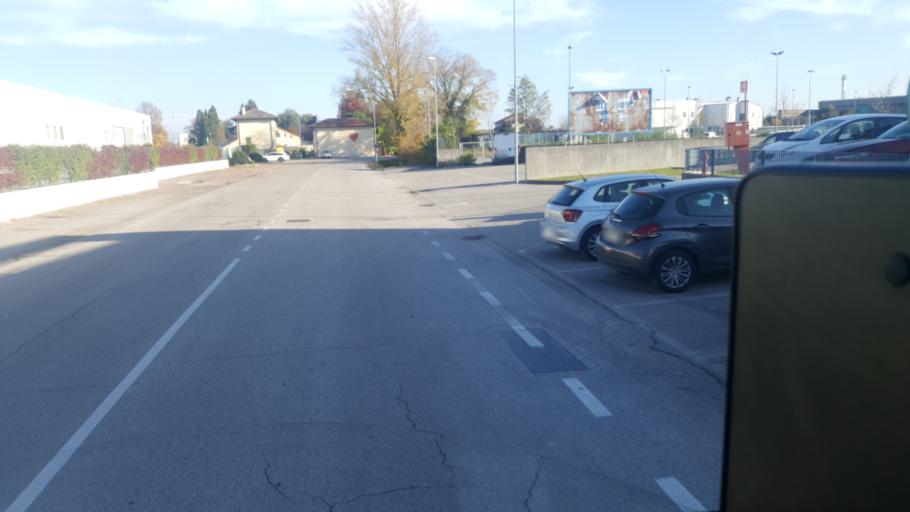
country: IT
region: Friuli Venezia Giulia
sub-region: Provincia di Pordenone
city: Azzano Decimo
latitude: 45.9290
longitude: 12.6552
